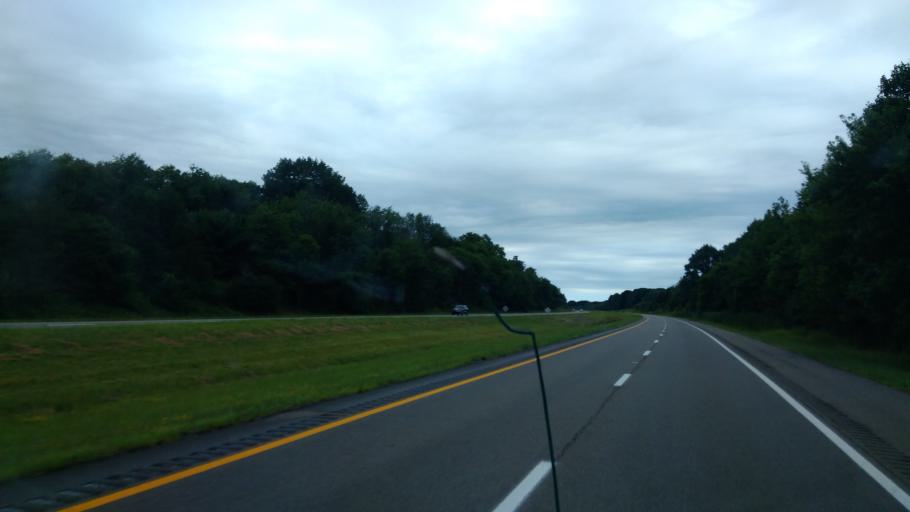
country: US
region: Ohio
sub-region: Mahoning County
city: Canfield
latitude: 40.9884
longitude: -80.7233
